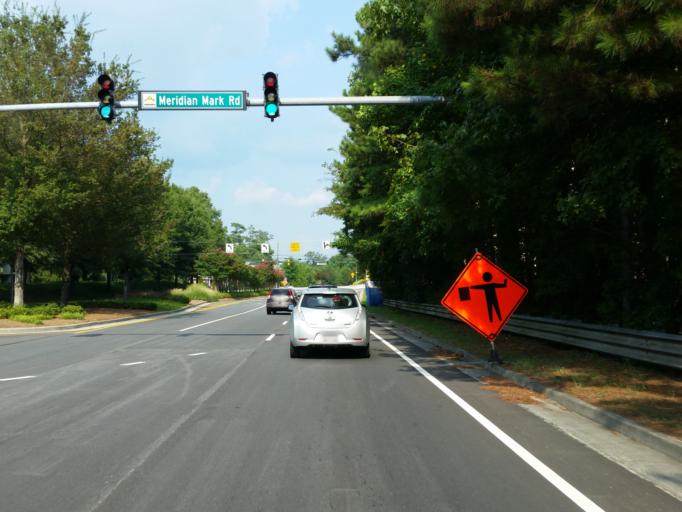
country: US
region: Georgia
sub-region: Fulton County
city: Sandy Springs
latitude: 33.9029
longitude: -84.3549
